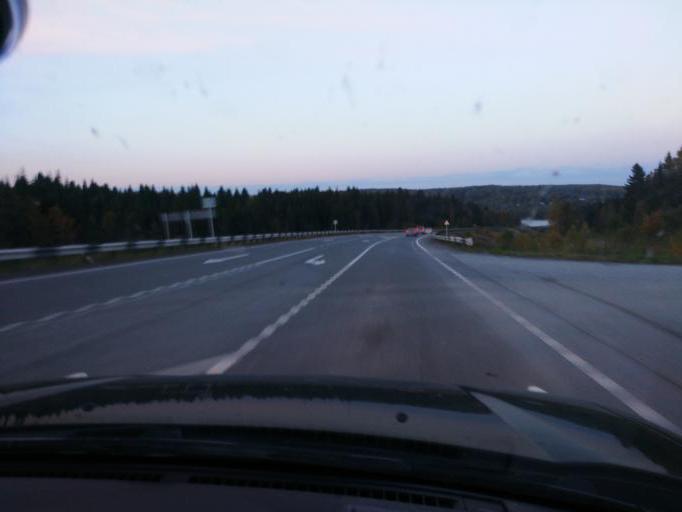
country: RU
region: Perm
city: Sylva
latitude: 58.2938
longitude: 56.8390
